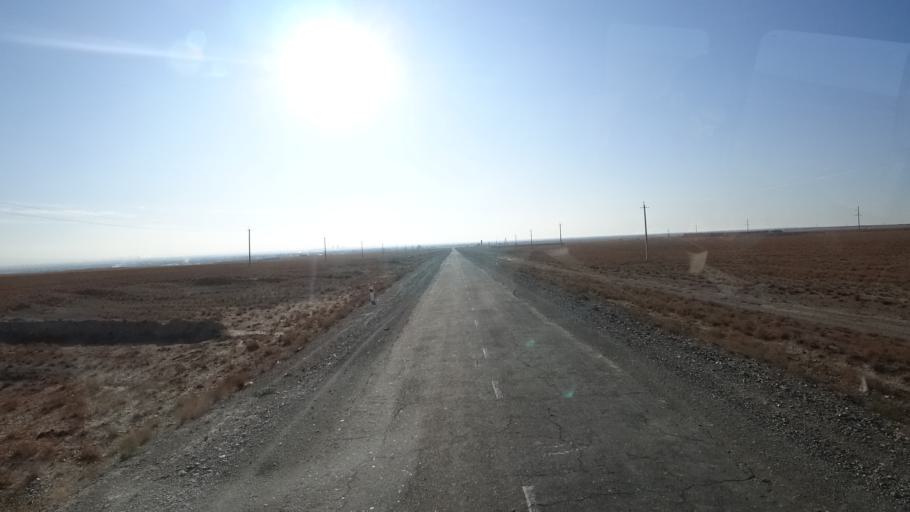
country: UZ
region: Navoiy
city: Beshrabot
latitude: 40.2283
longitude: 65.4048
